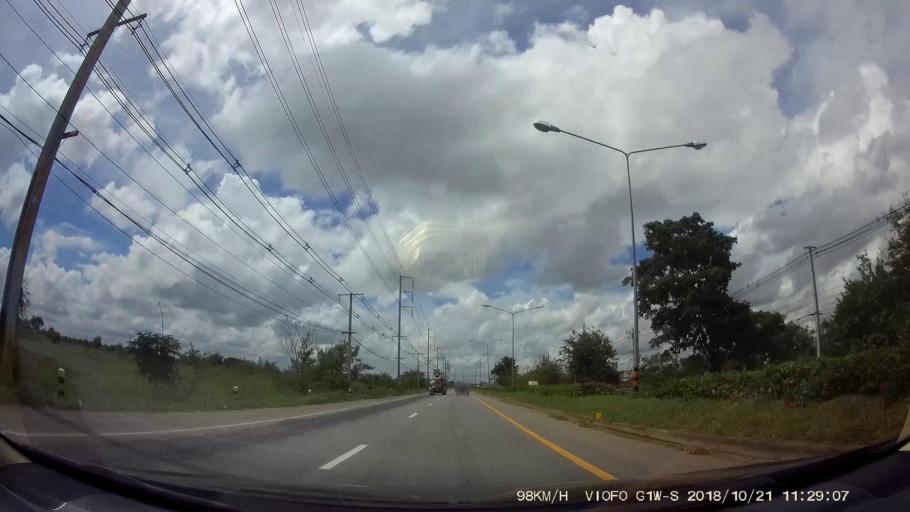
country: TH
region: Chaiyaphum
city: Chaiyaphum
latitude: 15.7871
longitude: 102.0350
